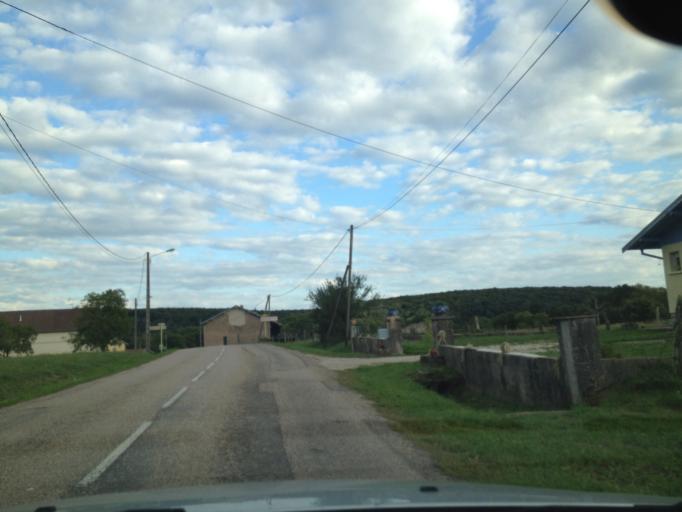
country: FR
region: Lorraine
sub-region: Departement des Vosges
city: Bains-les-Bains
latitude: 47.9748
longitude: 6.1727
